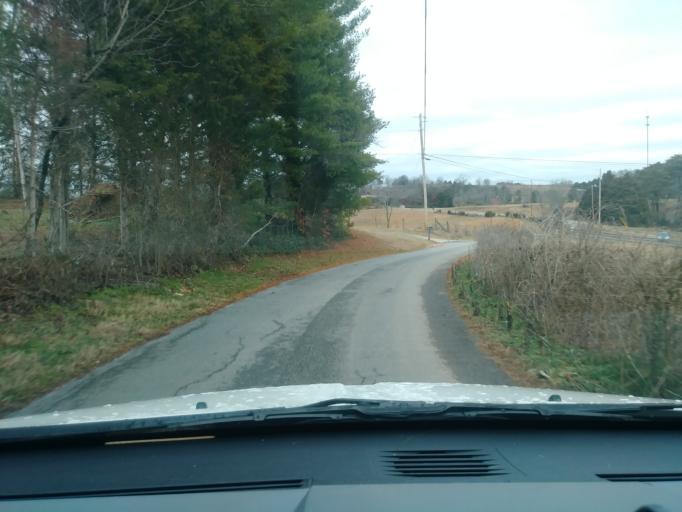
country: US
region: Tennessee
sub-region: Greene County
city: Greeneville
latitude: 36.0982
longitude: -82.8823
